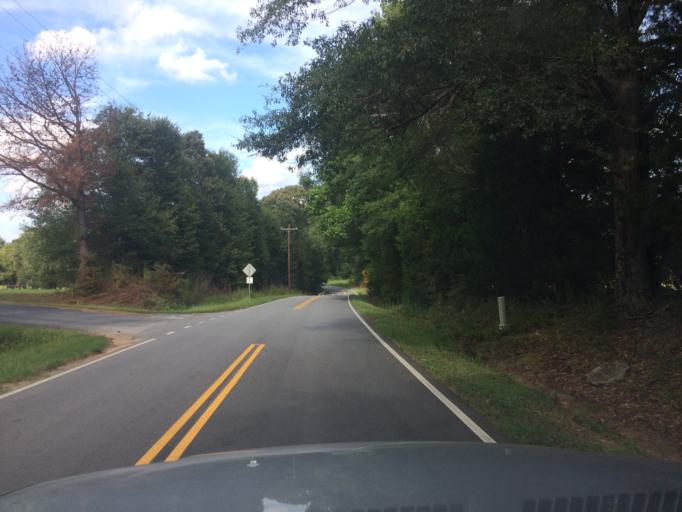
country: US
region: South Carolina
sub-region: Spartanburg County
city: Woodruff
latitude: 34.7396
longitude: -82.1169
